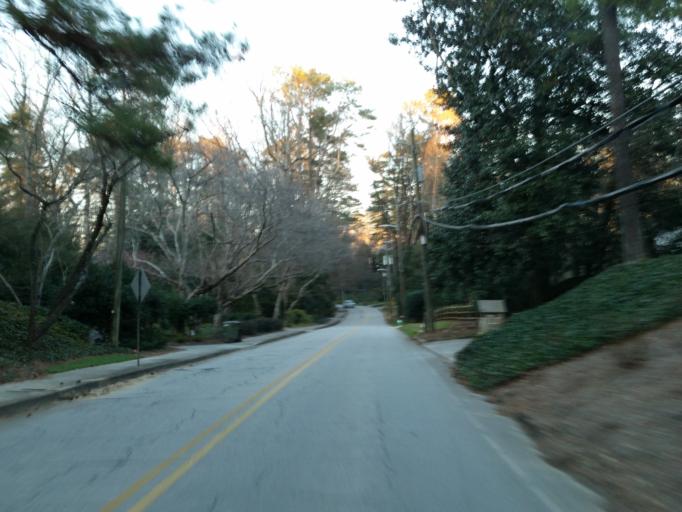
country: US
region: Georgia
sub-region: Cobb County
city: Vinings
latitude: 33.8313
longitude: -84.4311
